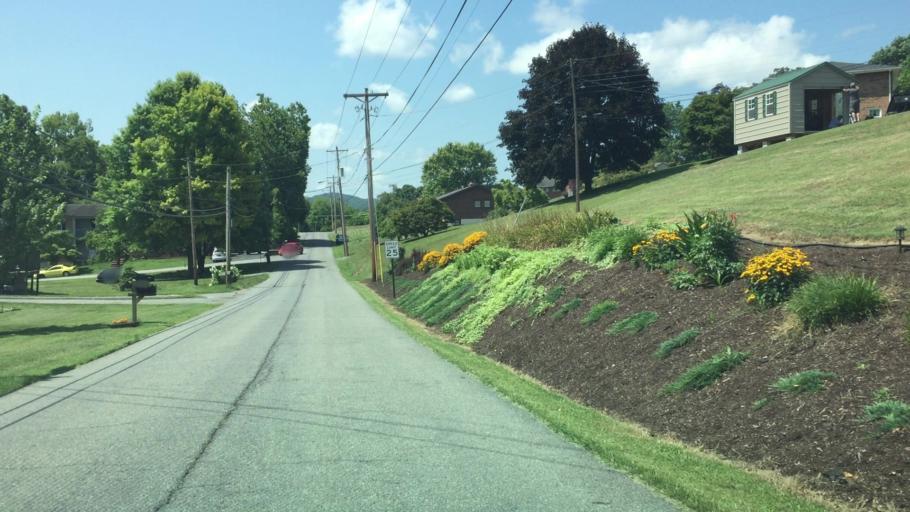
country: US
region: Virginia
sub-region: Pulaski County
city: Pulaski
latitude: 37.0584
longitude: -80.7502
